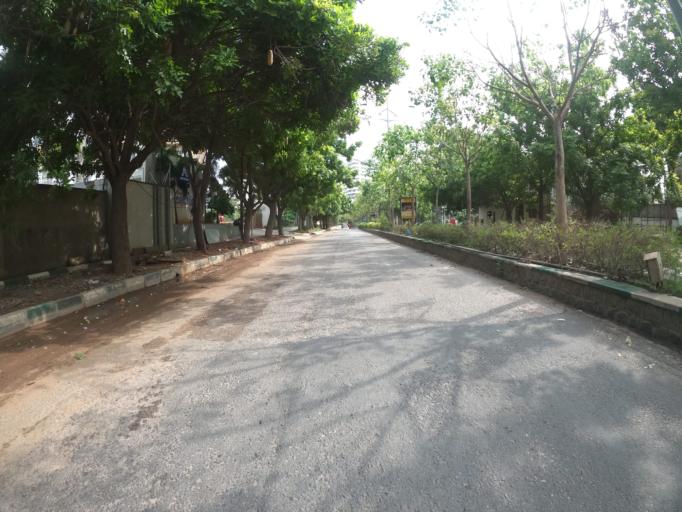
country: IN
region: Telangana
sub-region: Rangareddi
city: Kukatpalli
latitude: 17.4162
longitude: 78.3692
